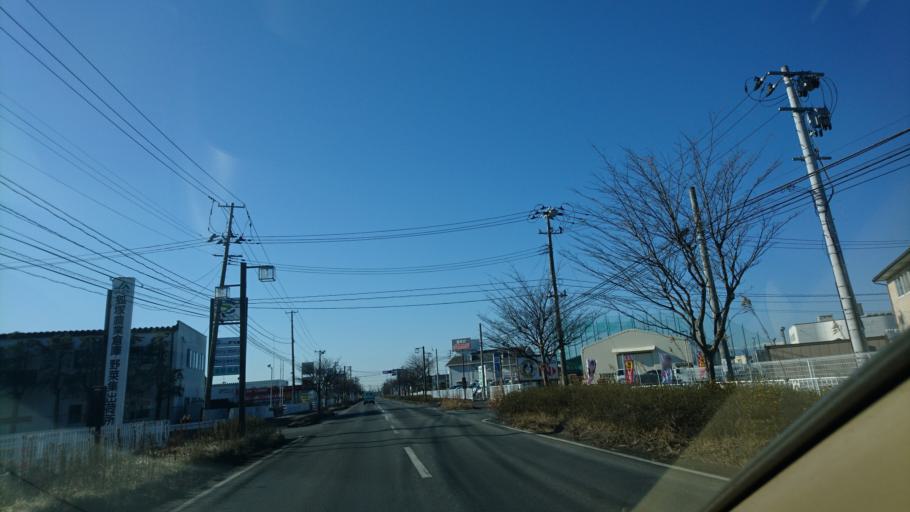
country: JP
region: Miyagi
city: Furukawa
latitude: 38.6028
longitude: 140.9795
